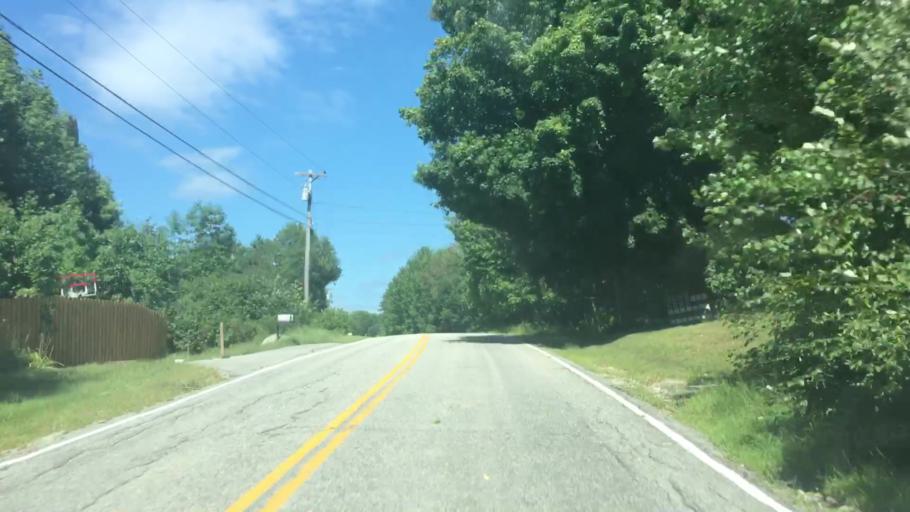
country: US
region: Maine
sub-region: Kennebec County
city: Monmouth
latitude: 44.1859
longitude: -69.9389
